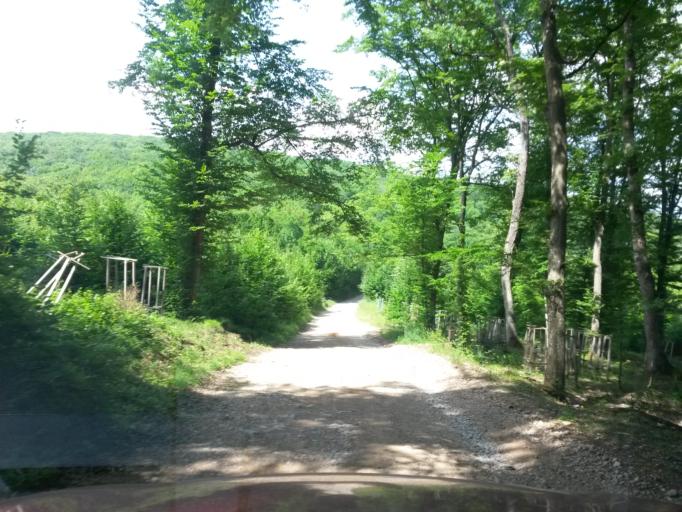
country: SK
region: Kosicky
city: Moldava nad Bodvou
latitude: 48.6453
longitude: 20.9582
